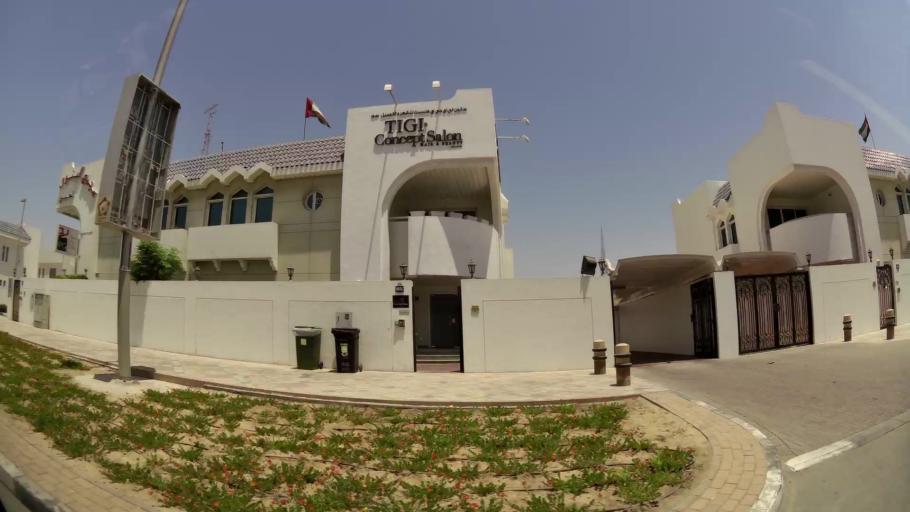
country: AE
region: Dubai
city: Dubai
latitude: 25.2183
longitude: 55.2531
